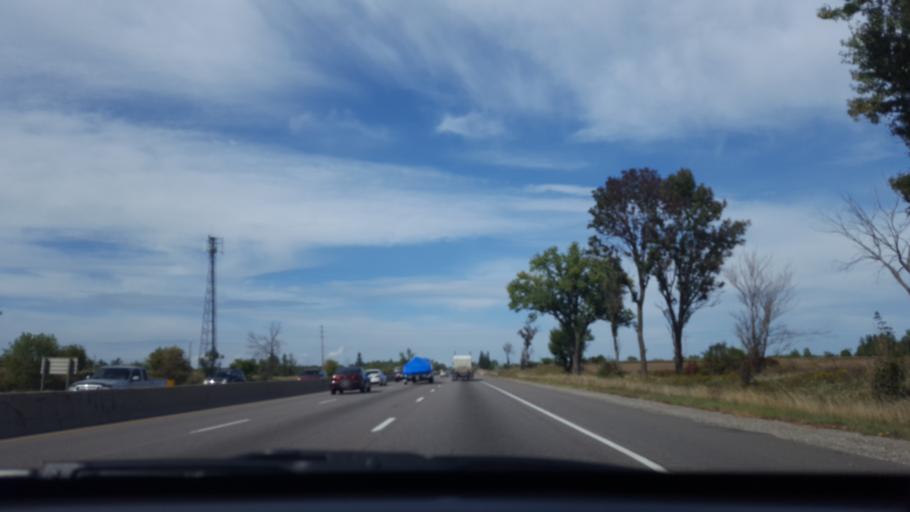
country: CA
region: Ontario
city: Vaughan
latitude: 43.8815
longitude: -79.5567
